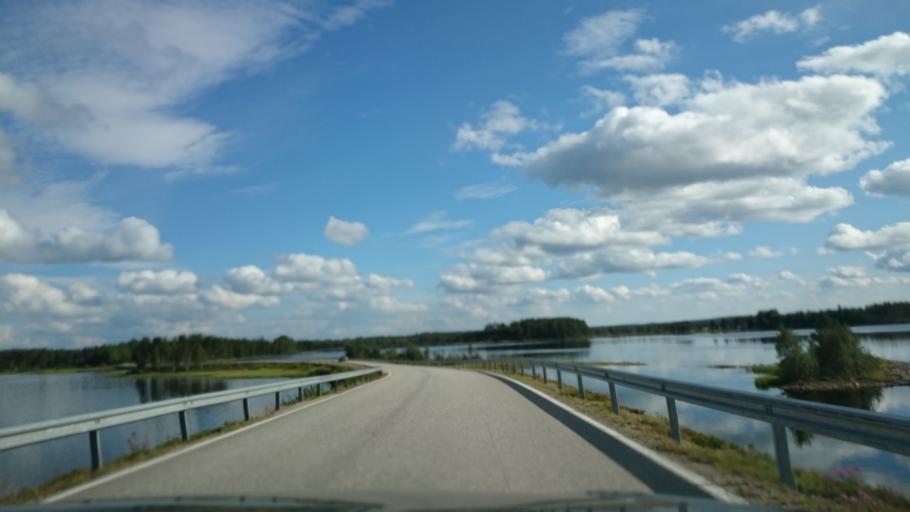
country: FI
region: Kainuu
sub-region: Kehys-Kainuu
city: Suomussalmi
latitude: 64.7633
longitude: 29.3727
